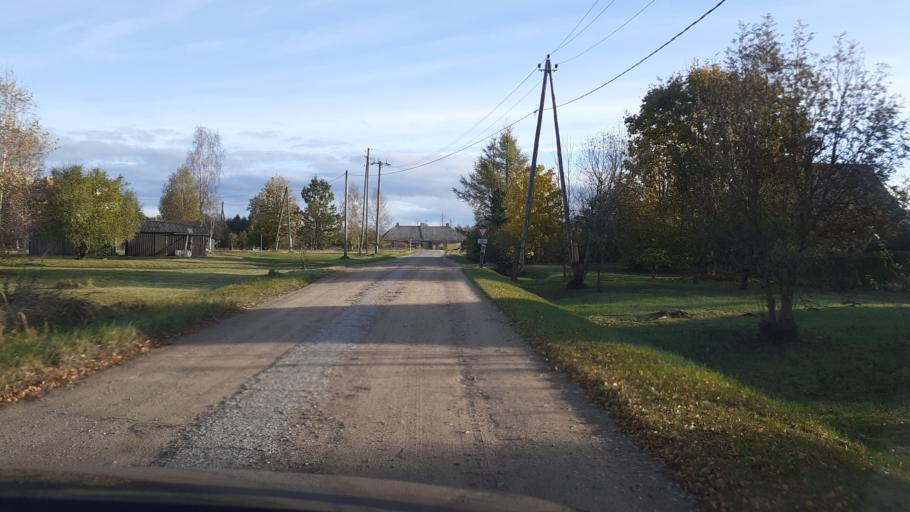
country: LV
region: Kuldigas Rajons
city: Kuldiga
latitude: 56.8806
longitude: 22.1120
